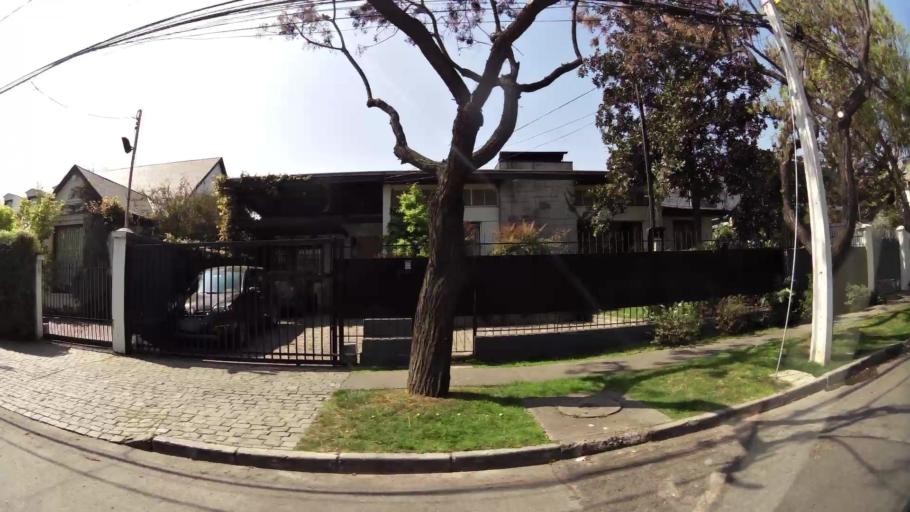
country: CL
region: Santiago Metropolitan
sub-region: Provincia de Santiago
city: Villa Presidente Frei, Nunoa, Santiago, Chile
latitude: -33.3928
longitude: -70.5896
